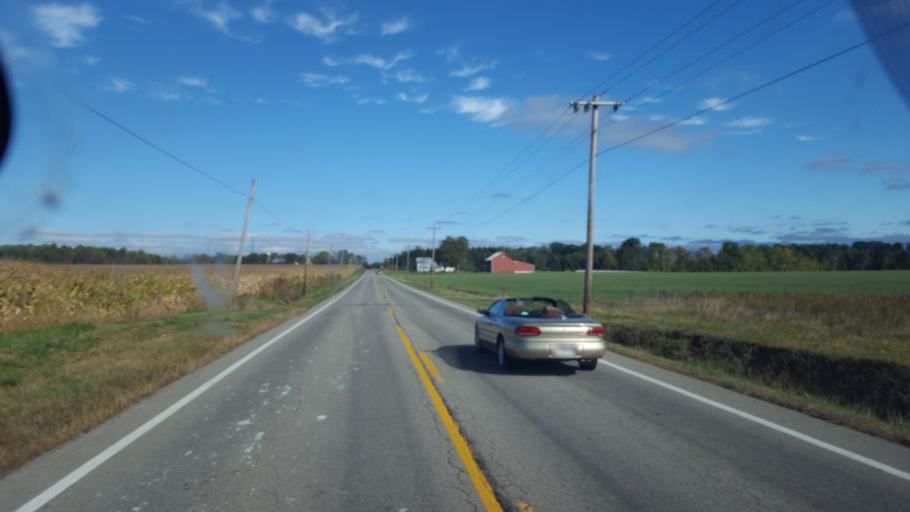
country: US
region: Ohio
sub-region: Huron County
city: Greenwich
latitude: 41.0800
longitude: -82.4873
